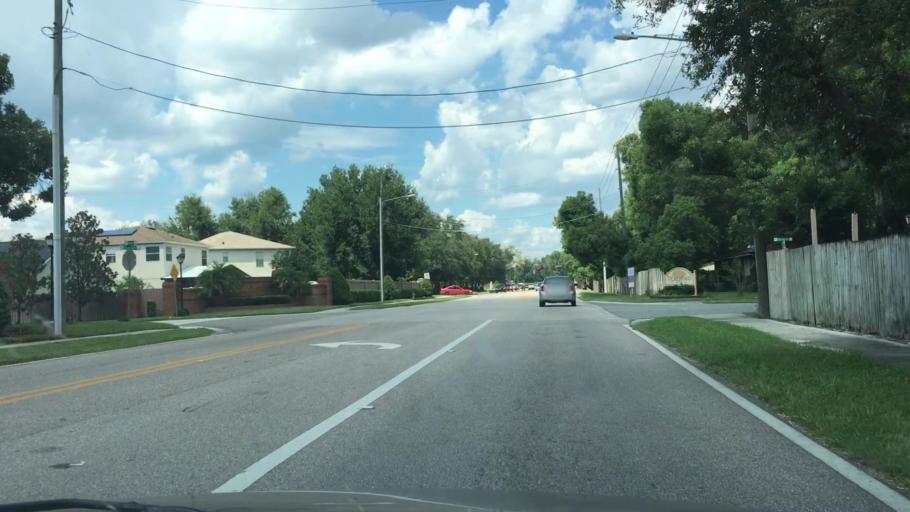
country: US
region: Florida
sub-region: Orange County
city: Lockhart
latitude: 28.6374
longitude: -81.4436
